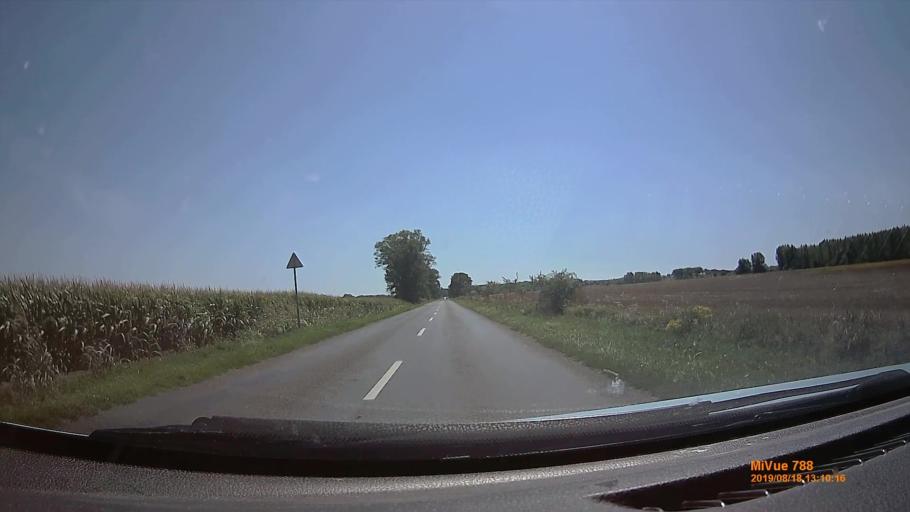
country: HU
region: Fejer
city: Kaloz
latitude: 46.9170
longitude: 18.5158
